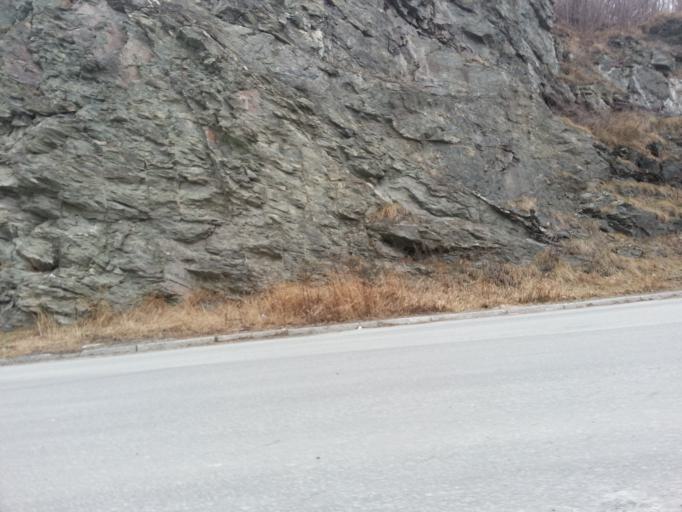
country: NO
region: Sor-Trondelag
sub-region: Trondheim
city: Trondheim
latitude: 63.4445
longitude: 10.4225
